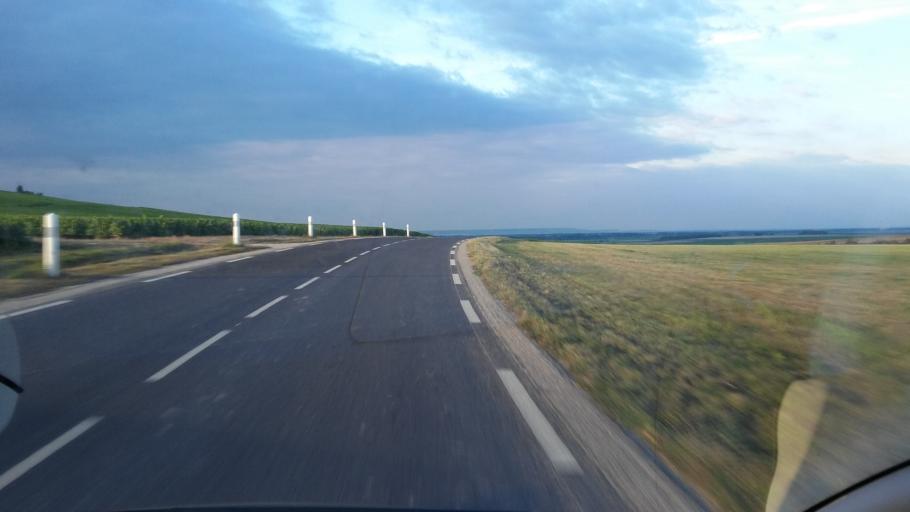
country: FR
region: Champagne-Ardenne
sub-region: Departement de la Marne
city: Vertus
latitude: 48.8559
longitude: 4.0021
